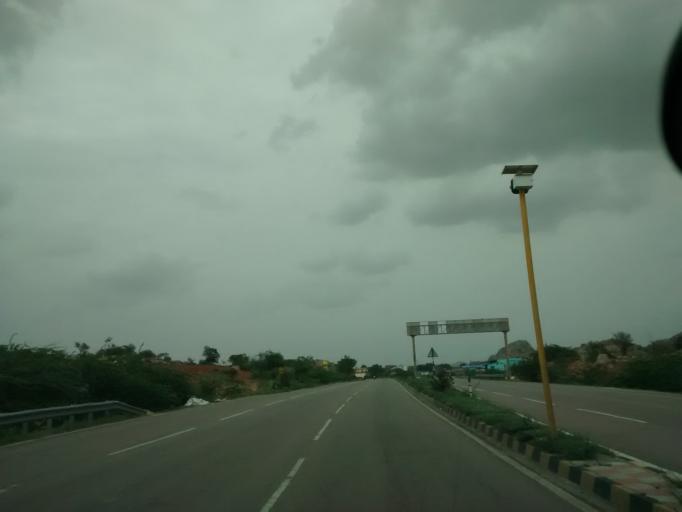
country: IN
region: Andhra Pradesh
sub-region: Kurnool
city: Ramapuram
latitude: 15.1554
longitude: 77.6680
